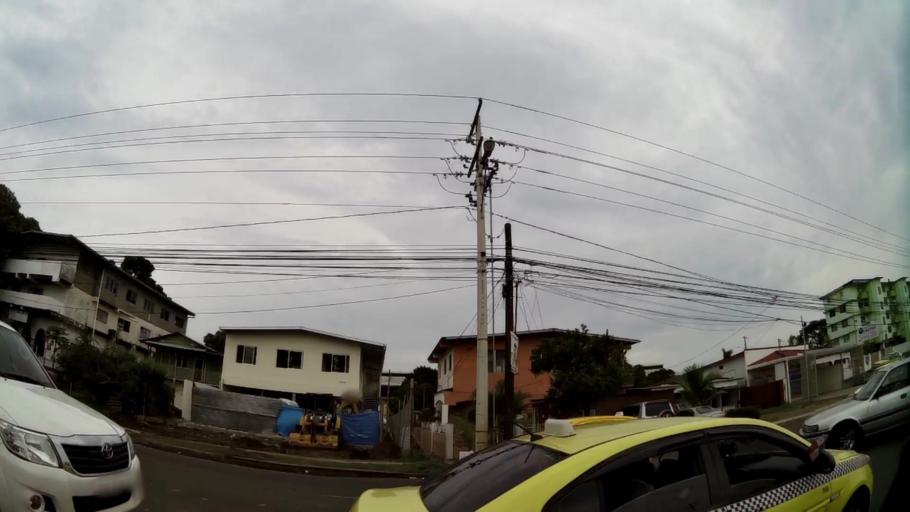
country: PA
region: Panama
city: San Miguelito
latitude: 9.0422
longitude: -79.4570
